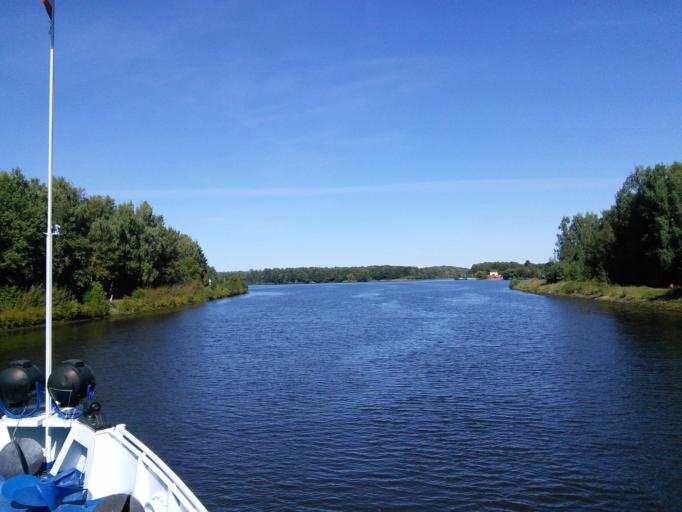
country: RU
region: Moskovskaya
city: Pirogovskiy
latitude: 56.0376
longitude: 37.6675
